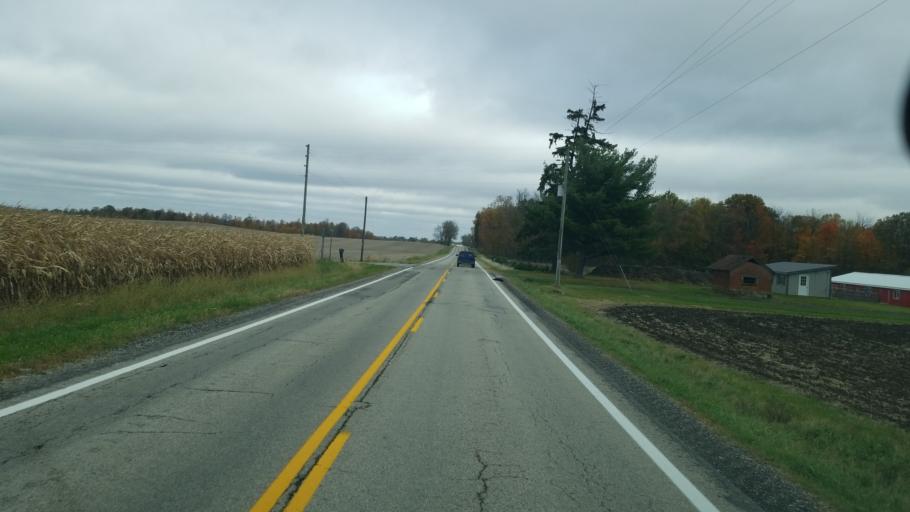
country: US
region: Ohio
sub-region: Crawford County
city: Bucyrus
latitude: 40.8633
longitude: -82.8553
